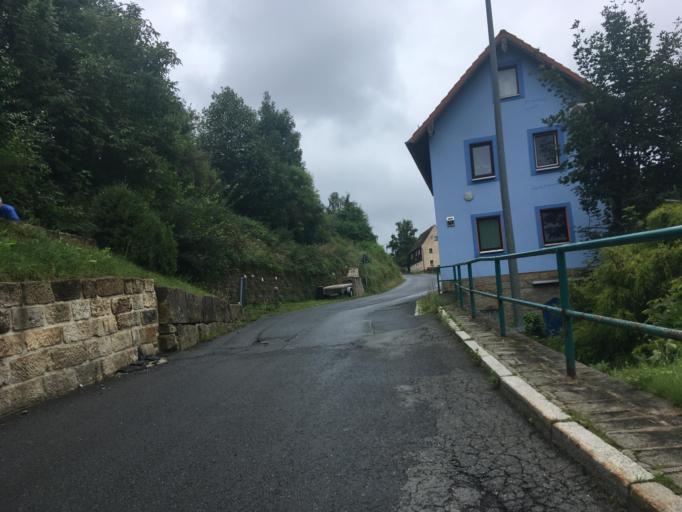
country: DE
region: Saxony
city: Bad Schandau
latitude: 50.8875
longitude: 14.2098
